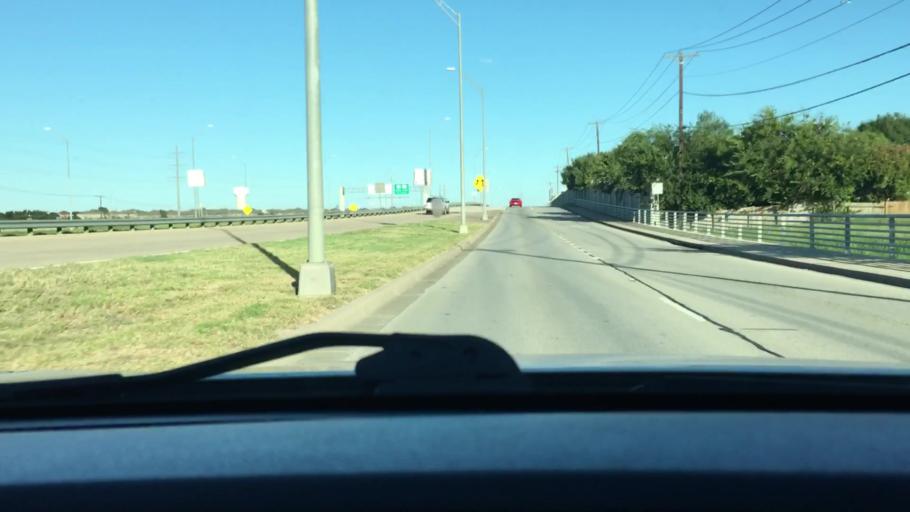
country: US
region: Texas
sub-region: Travis County
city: Windemere
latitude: 30.4882
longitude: -97.6339
